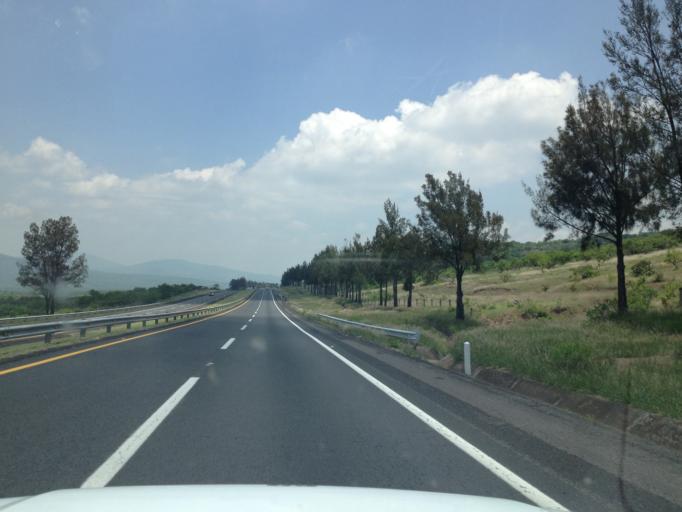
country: MX
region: Michoacan
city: Churintzio
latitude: 20.0935
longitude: -102.0155
